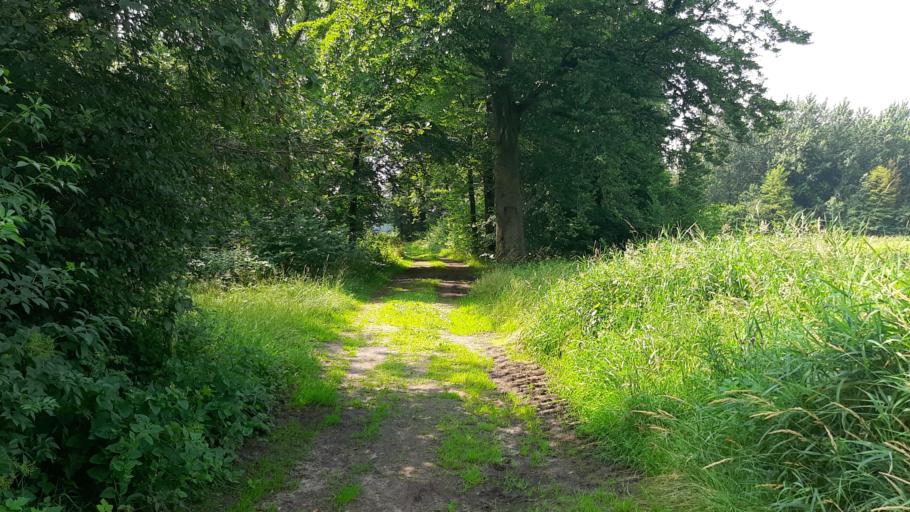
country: NL
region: Gelderland
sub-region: Gemeente Rheden
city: Spankeren
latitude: 52.0788
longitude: 6.1245
